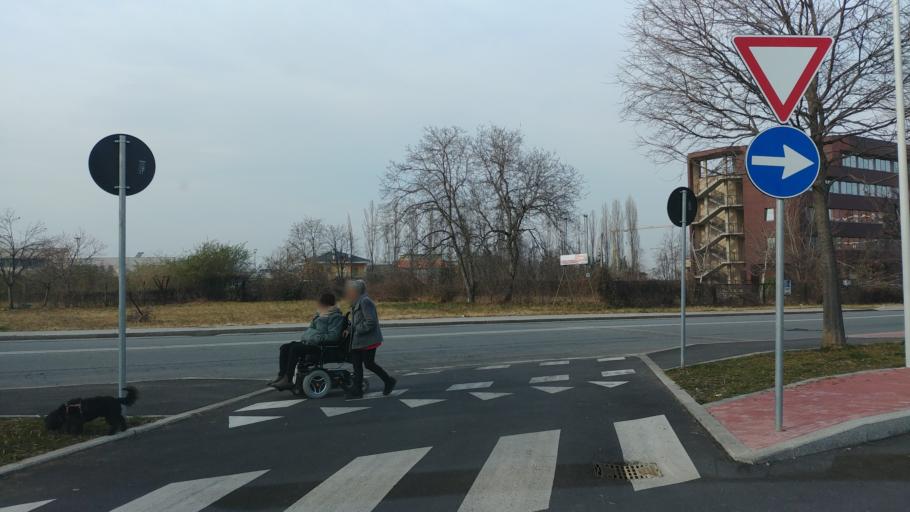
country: IT
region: Piedmont
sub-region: Provincia di Cuneo
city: Cuneo
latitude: 44.3761
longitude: 7.5262
